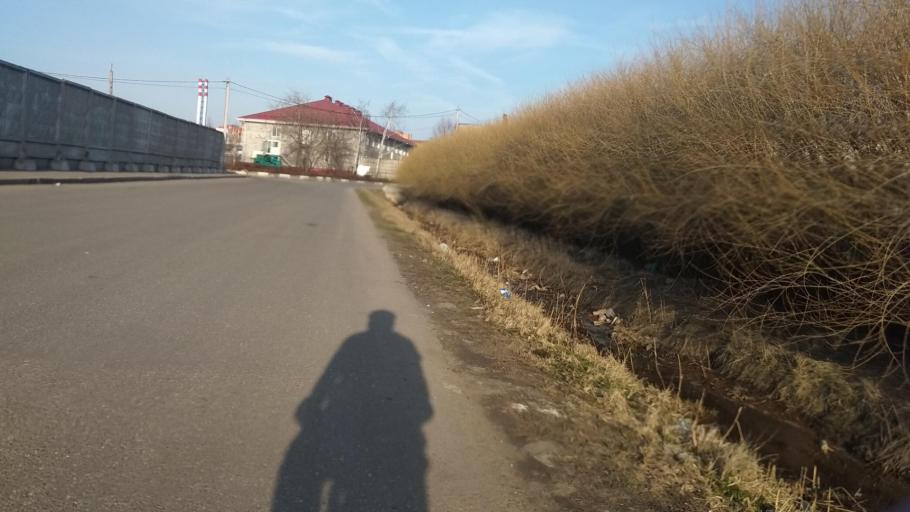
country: RU
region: Moskovskaya
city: Razvilka
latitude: 55.5816
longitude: 37.7155
